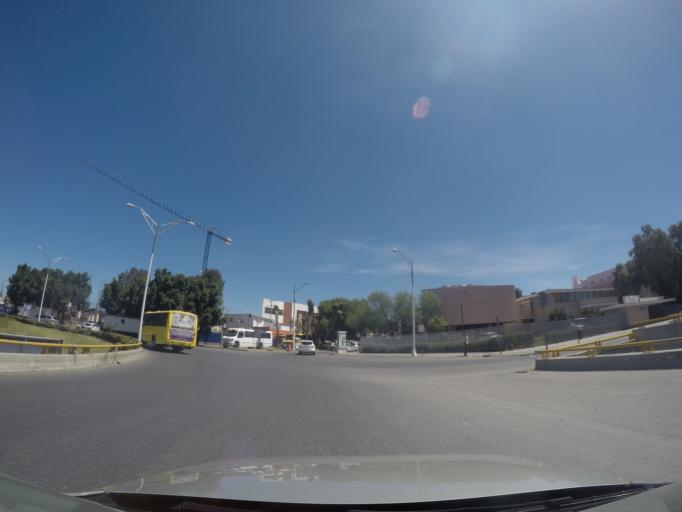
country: MX
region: San Luis Potosi
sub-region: San Luis Potosi
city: San Luis Potosi
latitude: 22.1485
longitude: -101.0153
